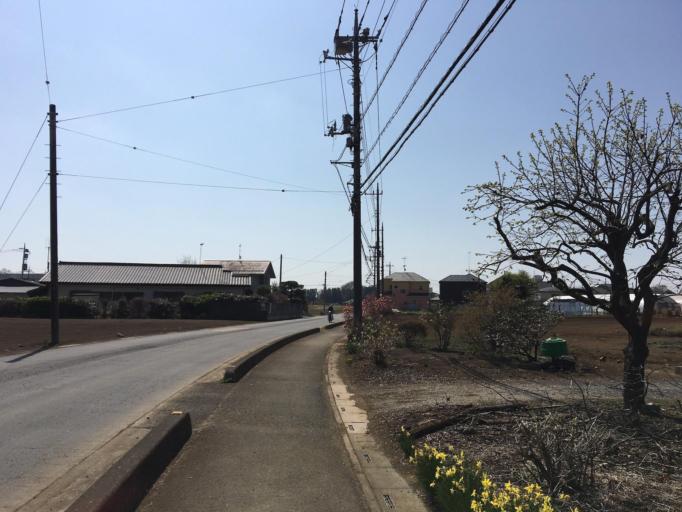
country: JP
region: Saitama
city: Sakado
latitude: 35.9189
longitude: 139.3613
